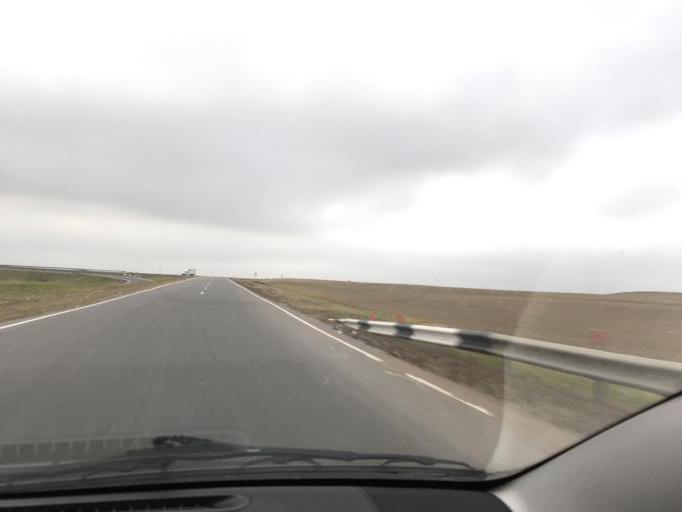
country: BY
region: Vitebsk
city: Vitebsk
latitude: 55.1558
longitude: 30.0694
